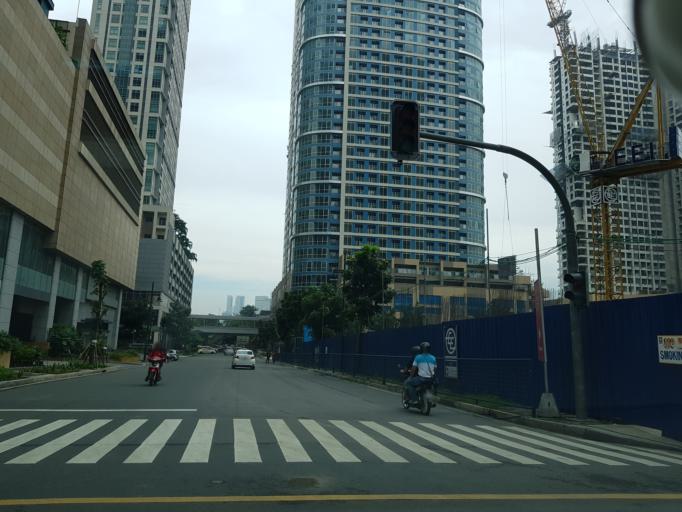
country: PH
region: Metro Manila
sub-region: Makati City
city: Makati City
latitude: 14.5569
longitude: 121.0555
